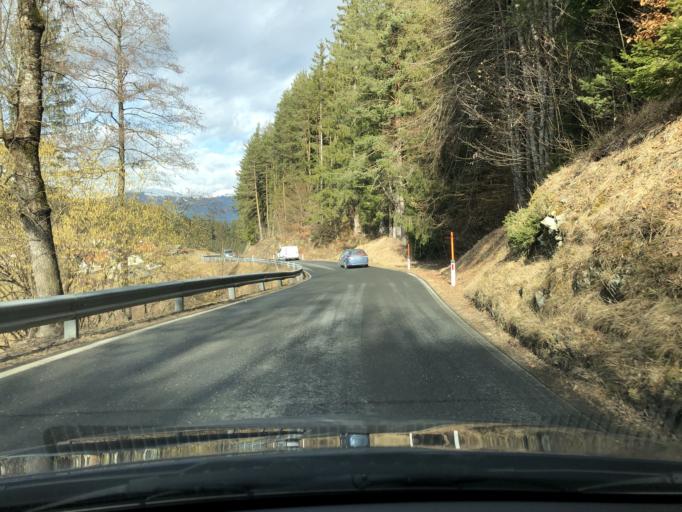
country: AT
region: Carinthia
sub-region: Politischer Bezirk Villach Land
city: Paternion
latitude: 46.7113
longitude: 13.6105
